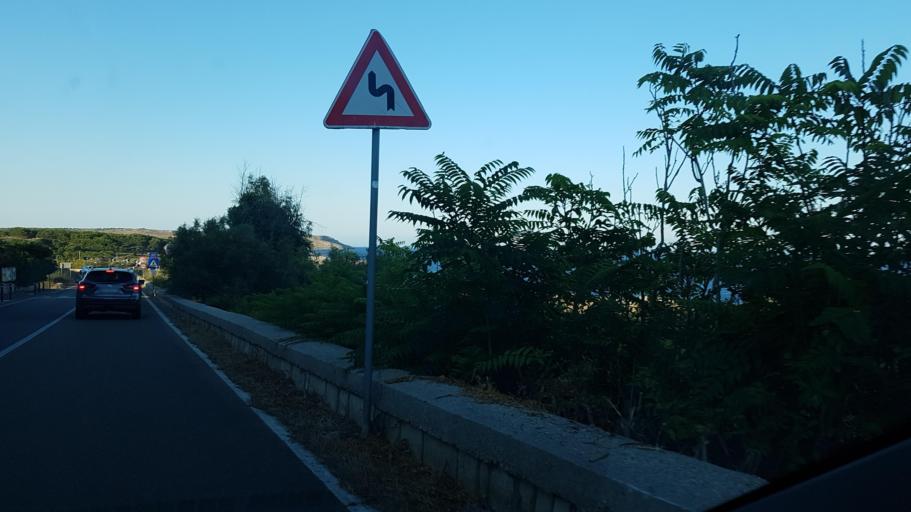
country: IT
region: Apulia
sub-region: Provincia di Lecce
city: Cerfignano
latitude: 40.0747
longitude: 18.4815
